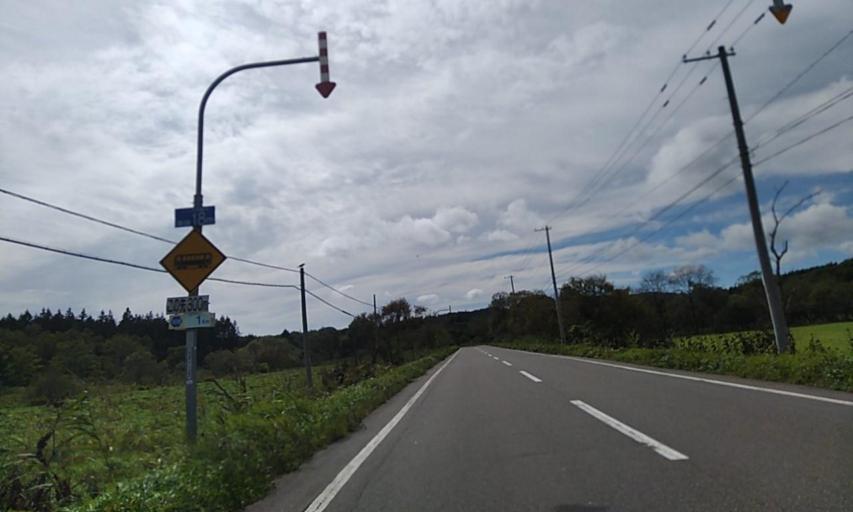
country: JP
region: Hokkaido
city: Kushiro
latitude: 42.8458
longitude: 143.8448
